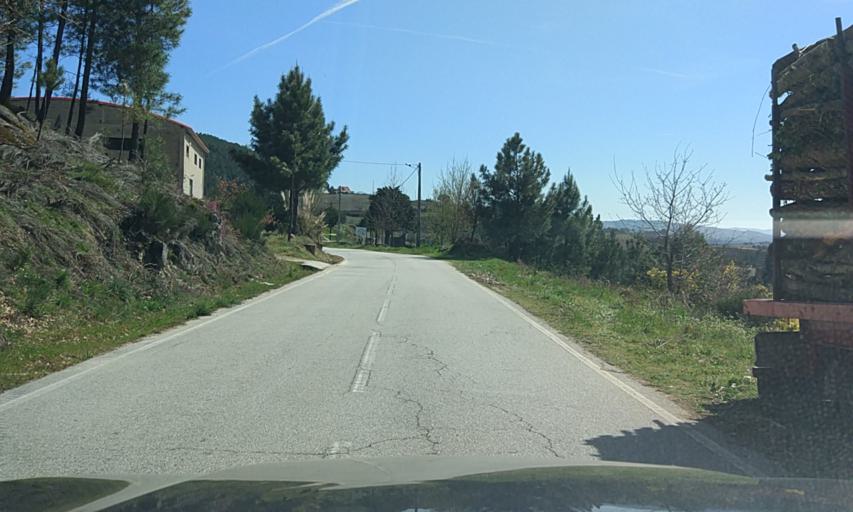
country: PT
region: Vila Real
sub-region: Sabrosa
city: Sabrosa
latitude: 41.3357
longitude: -7.5786
